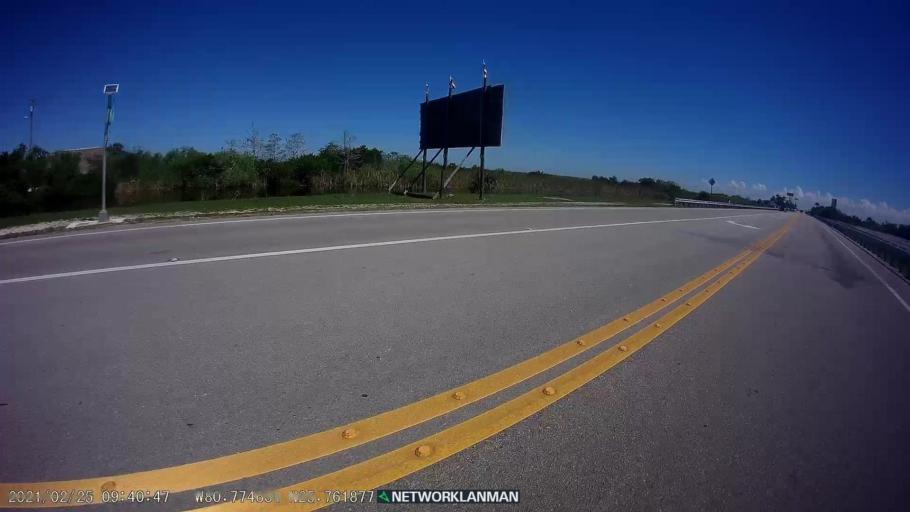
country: US
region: Florida
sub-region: Miami-Dade County
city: Kendall West
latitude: 25.7615
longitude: -80.7744
